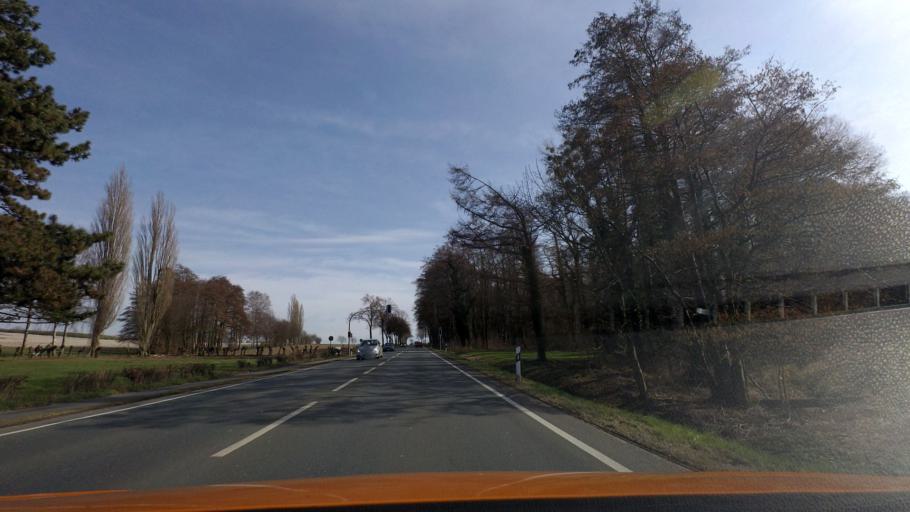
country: DE
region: Lower Saxony
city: Bad Nenndorf
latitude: 52.3288
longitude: 9.3846
